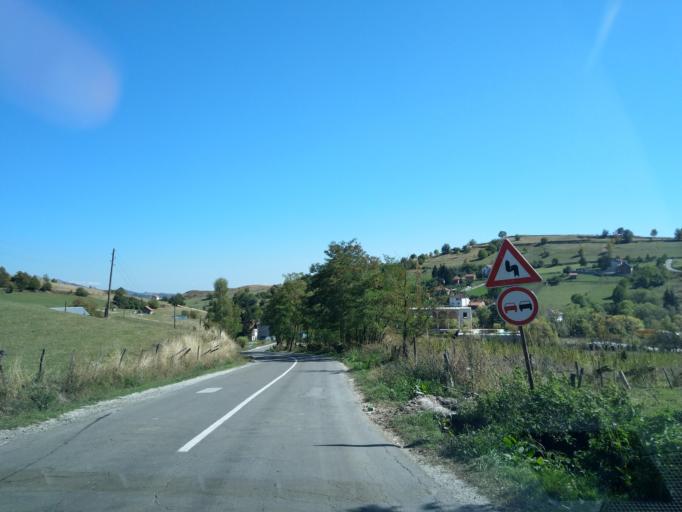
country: RS
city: Sokolovica
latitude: 43.2493
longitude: 20.2298
